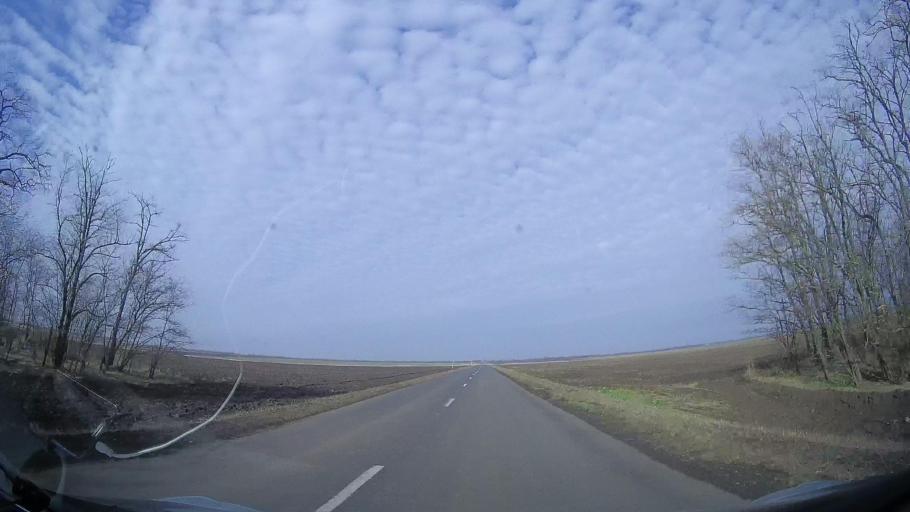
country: RU
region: Rostov
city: Gigant
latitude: 46.8774
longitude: 41.2714
